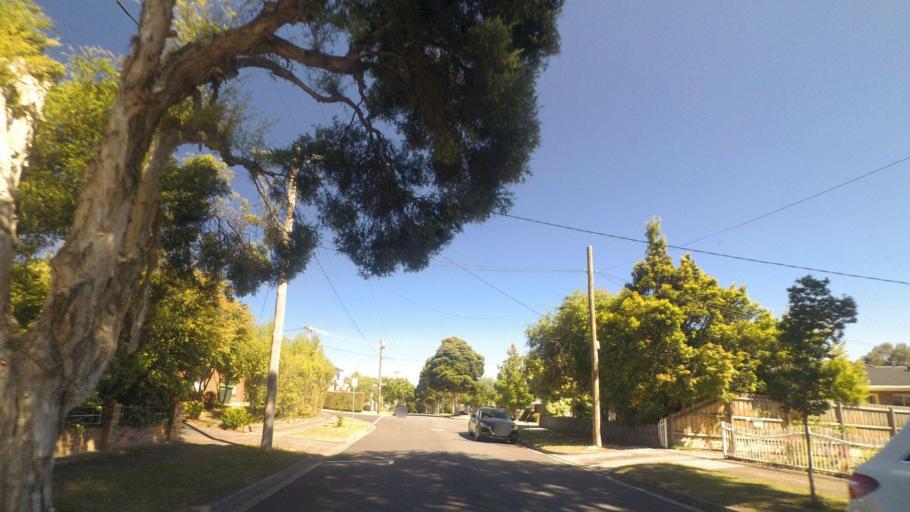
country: AU
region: Victoria
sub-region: Manningham
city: Donvale
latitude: -37.8004
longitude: 145.1813
